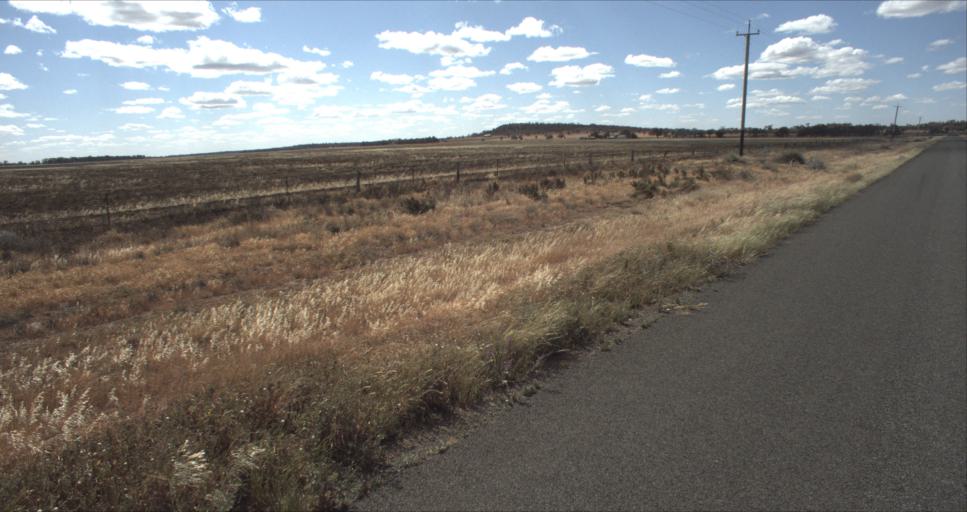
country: AU
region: New South Wales
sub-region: Leeton
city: Leeton
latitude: -34.4359
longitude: 146.2573
